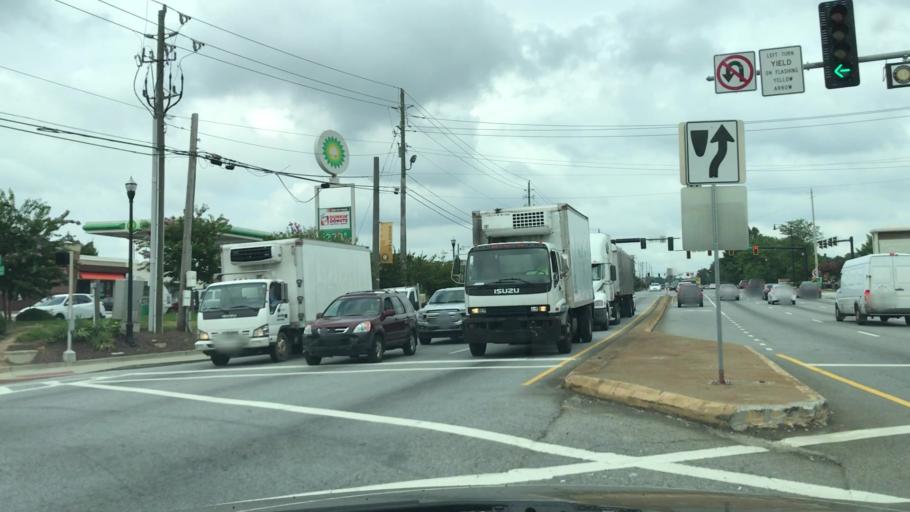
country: US
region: Georgia
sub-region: Gwinnett County
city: Duluth
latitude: 33.9543
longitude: -84.1314
